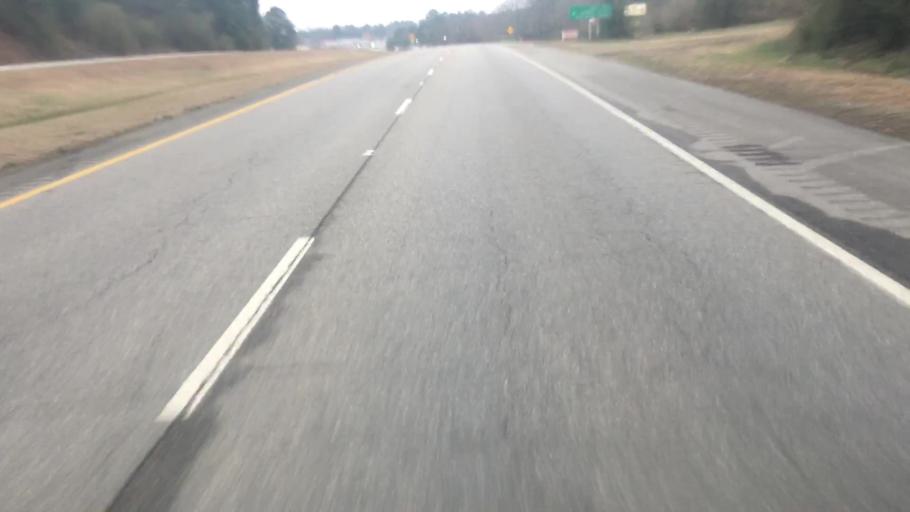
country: US
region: Alabama
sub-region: Walker County
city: Sumiton
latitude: 33.7652
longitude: -87.0698
